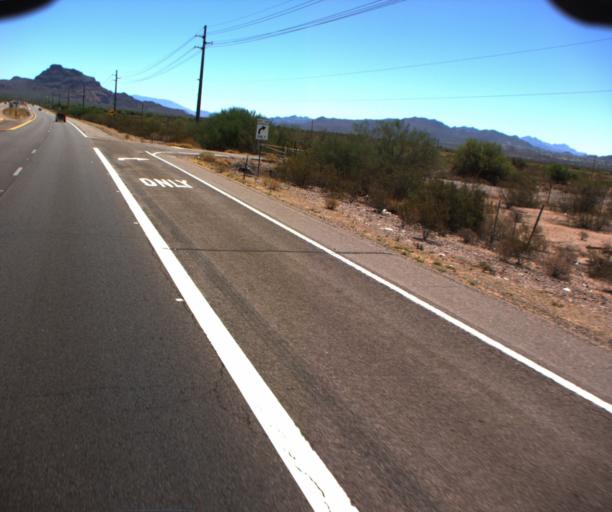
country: US
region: Arizona
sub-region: Maricopa County
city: Mesa
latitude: 33.5106
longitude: -111.7624
